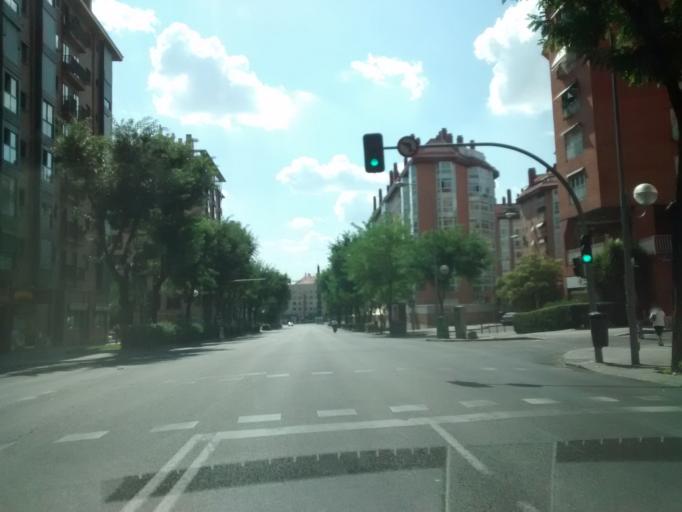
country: ES
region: Madrid
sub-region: Provincia de Madrid
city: Arganzuela
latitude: 40.4036
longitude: -3.7077
